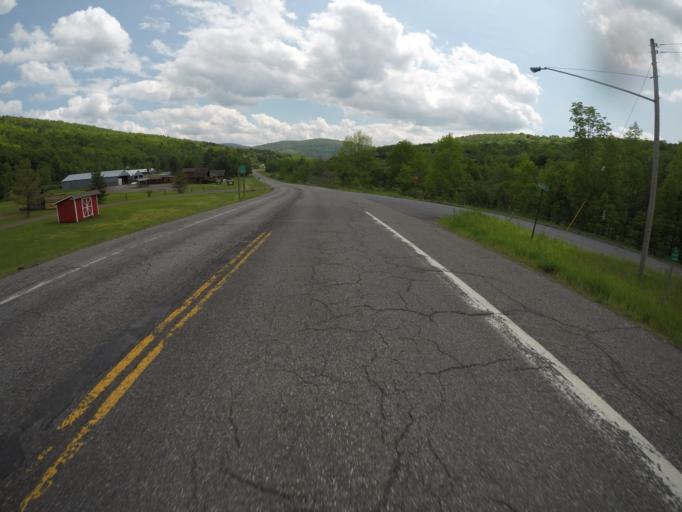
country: US
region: New York
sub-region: Delaware County
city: Stamford
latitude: 42.2027
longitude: -74.5997
